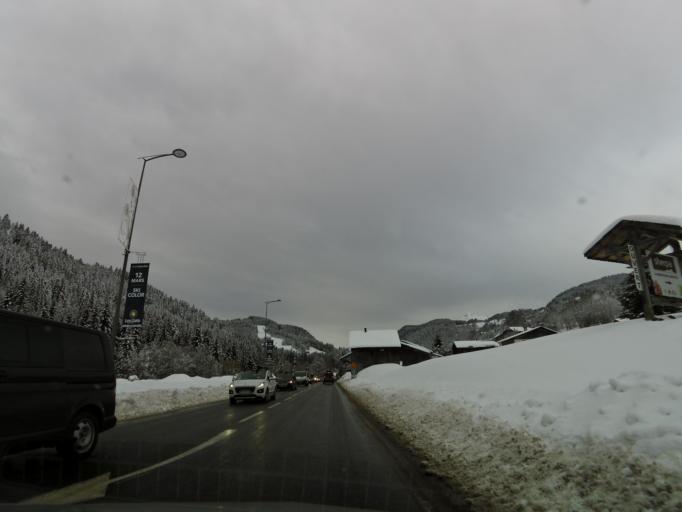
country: FR
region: Rhone-Alpes
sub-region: Departement de la Haute-Savoie
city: Les Gets
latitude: 46.1477
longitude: 6.6556
